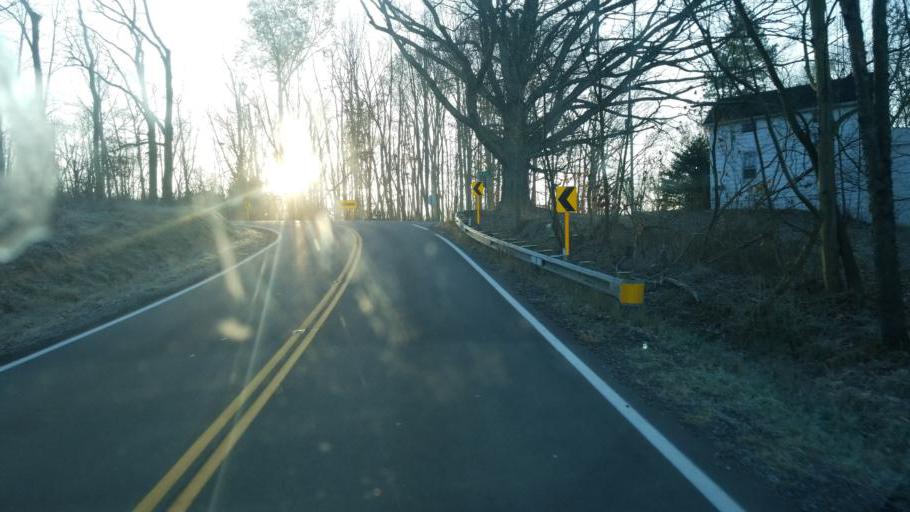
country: US
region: Ohio
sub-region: Medina County
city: Medina
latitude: 41.0997
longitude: -81.7854
